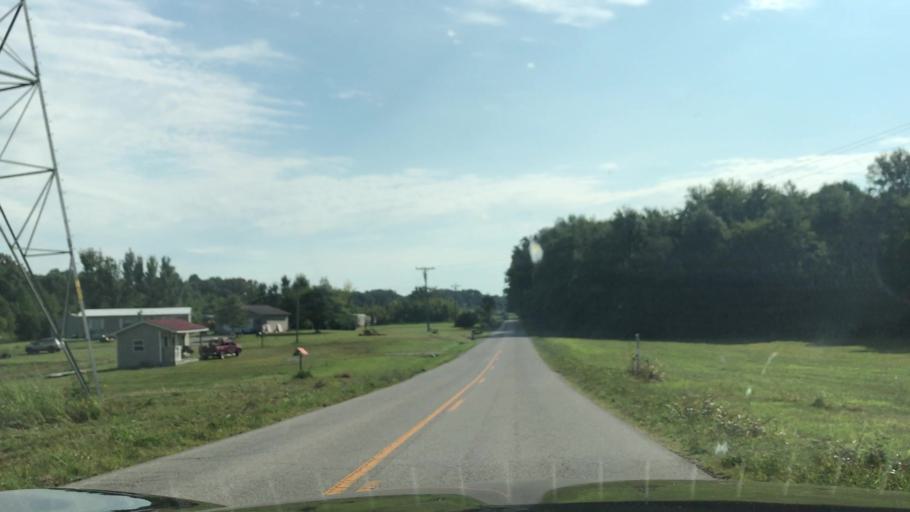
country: US
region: Kentucky
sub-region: Hart County
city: Munfordville
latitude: 37.2289
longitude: -85.7140
